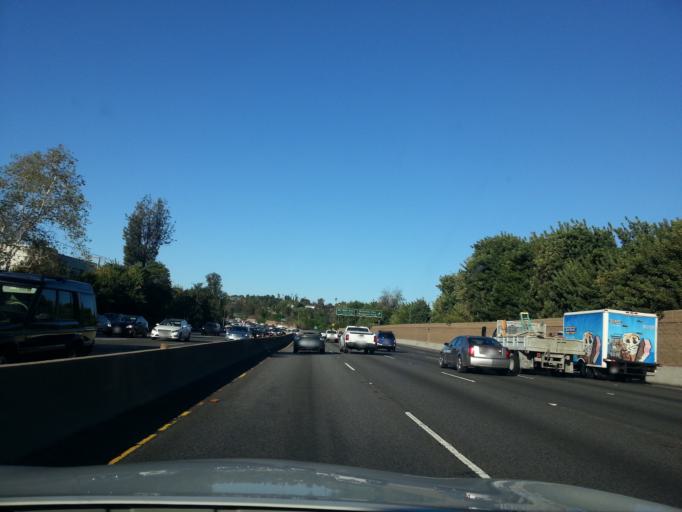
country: US
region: California
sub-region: Los Angeles County
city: Woodland Hills
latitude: 34.1732
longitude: -118.5658
